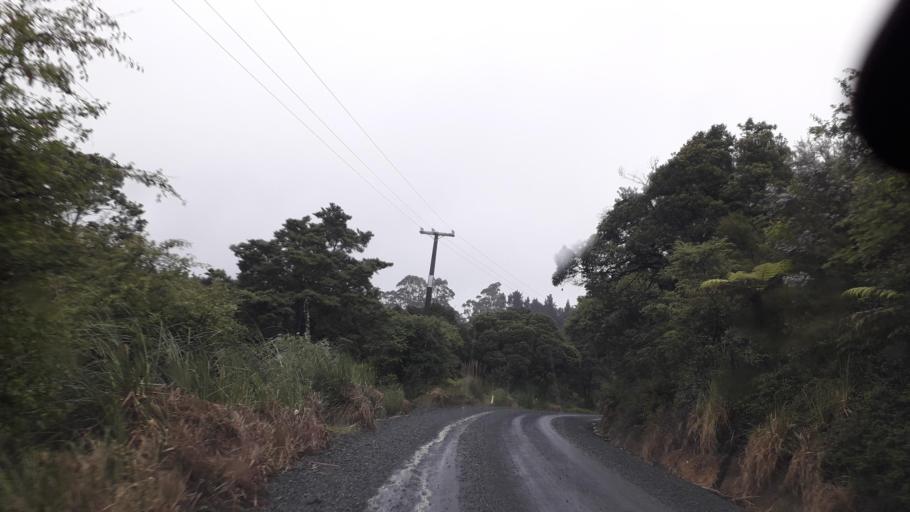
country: NZ
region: Northland
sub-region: Far North District
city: Kerikeri
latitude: -35.1162
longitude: 173.7533
